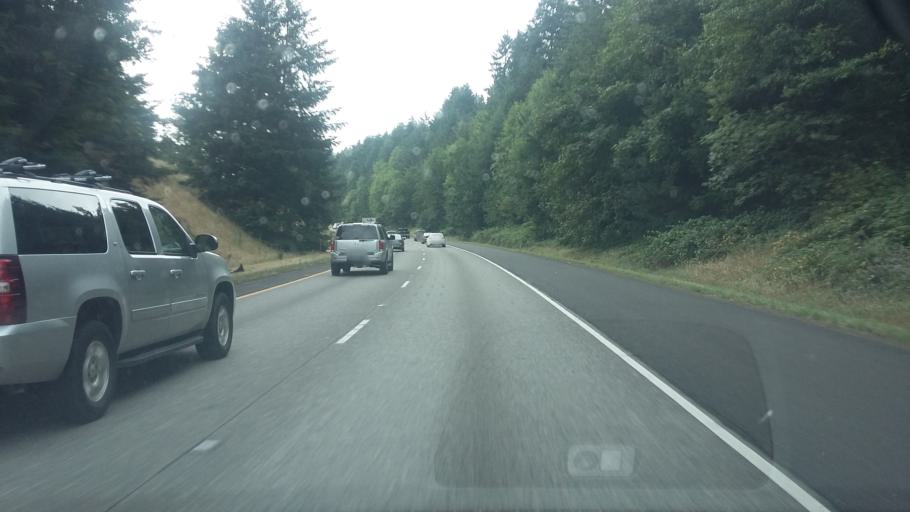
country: US
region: Washington
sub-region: Clark County
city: Salmon Creek
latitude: 45.7015
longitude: -122.6264
